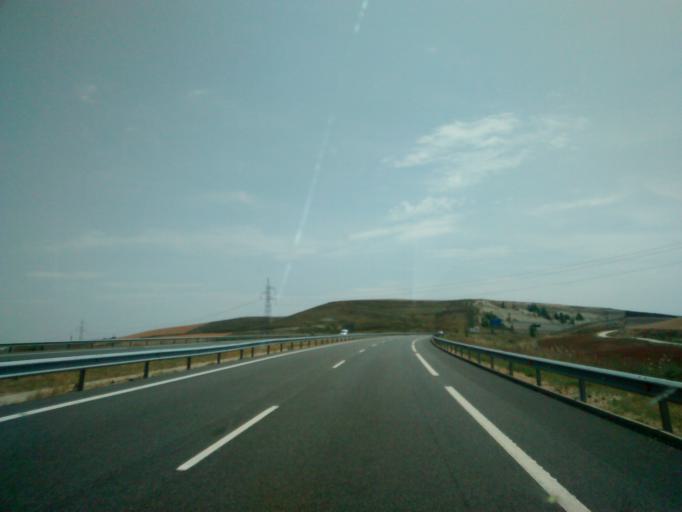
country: ES
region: Castille and Leon
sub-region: Provincia de Burgos
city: Tardajos
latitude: 42.3606
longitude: -3.8101
